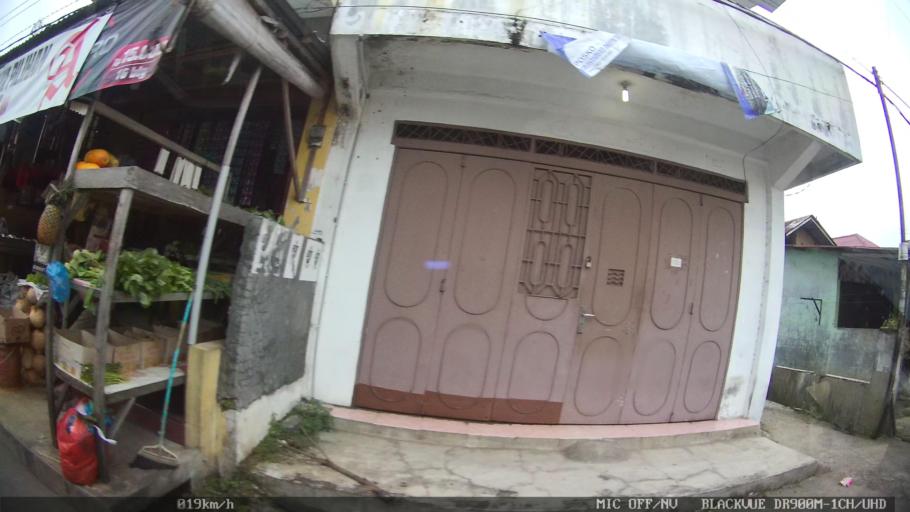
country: ID
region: North Sumatra
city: Deli Tua
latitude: 3.5433
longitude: 98.7064
